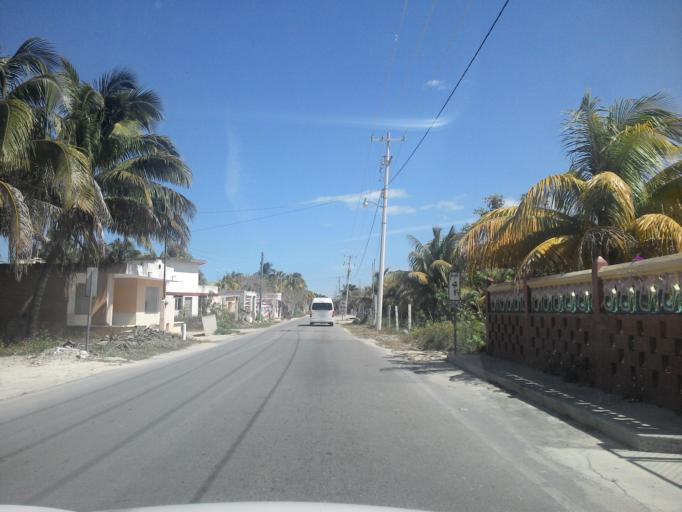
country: MX
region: Yucatan
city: Telchac Puerto
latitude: 21.3412
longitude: -89.2774
